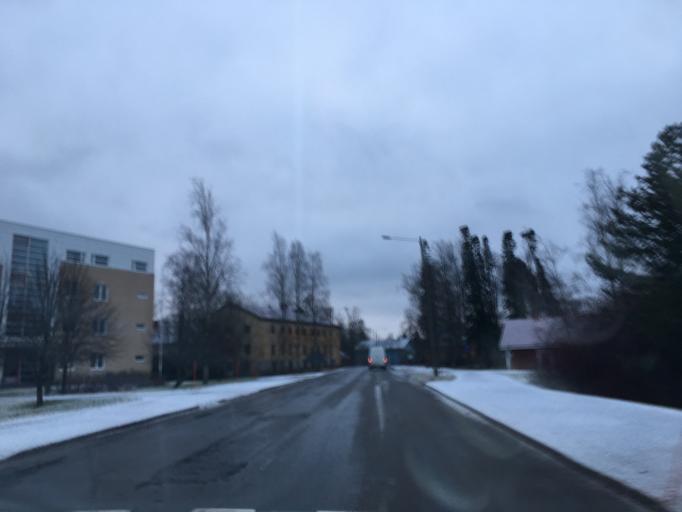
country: FI
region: Varsinais-Suomi
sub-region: Loimaa
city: Aura
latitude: 60.6453
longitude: 22.5910
